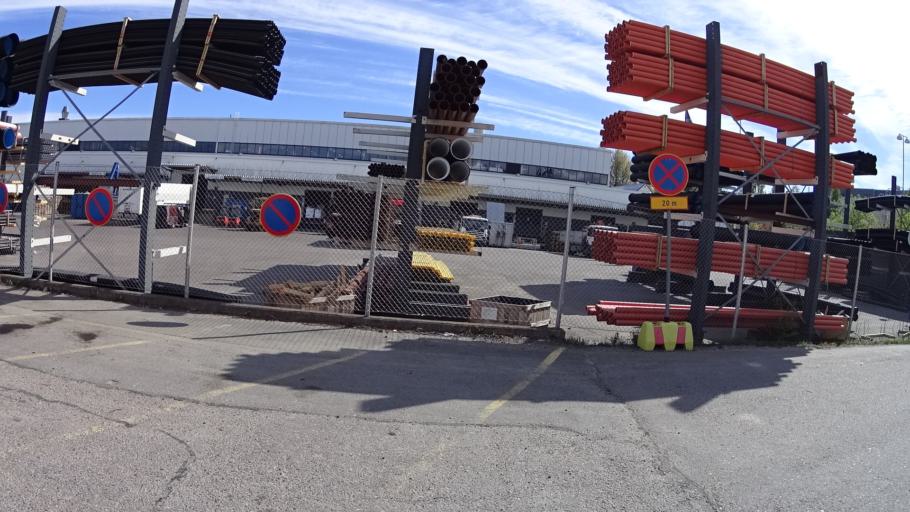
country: FI
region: Uusimaa
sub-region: Helsinki
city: Vantaa
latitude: 60.2983
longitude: 24.9644
